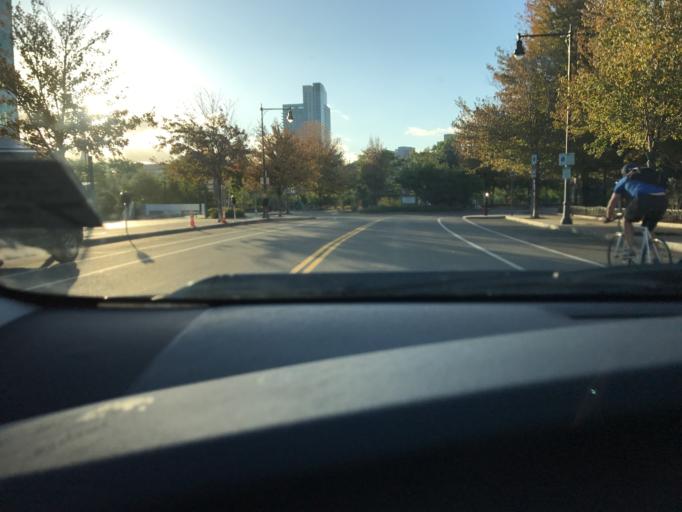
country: US
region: Massachusetts
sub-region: Suffolk County
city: Boston
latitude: 42.3698
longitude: -71.0697
